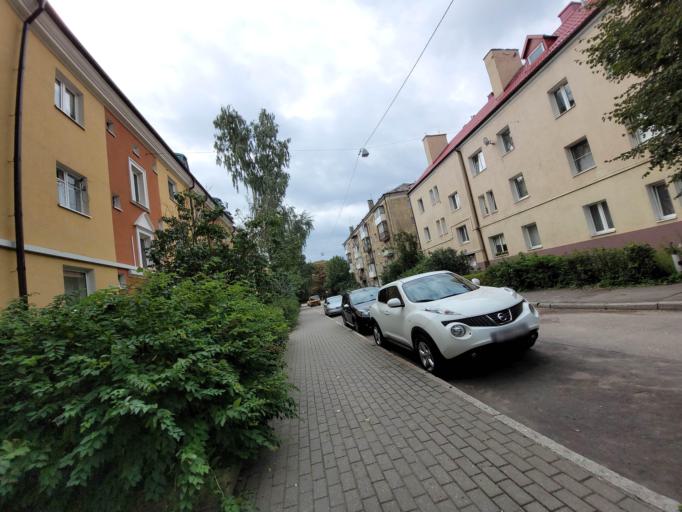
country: RU
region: Kaliningrad
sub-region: Gorod Kaliningrad
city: Kaliningrad
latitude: 54.6962
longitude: 20.5138
